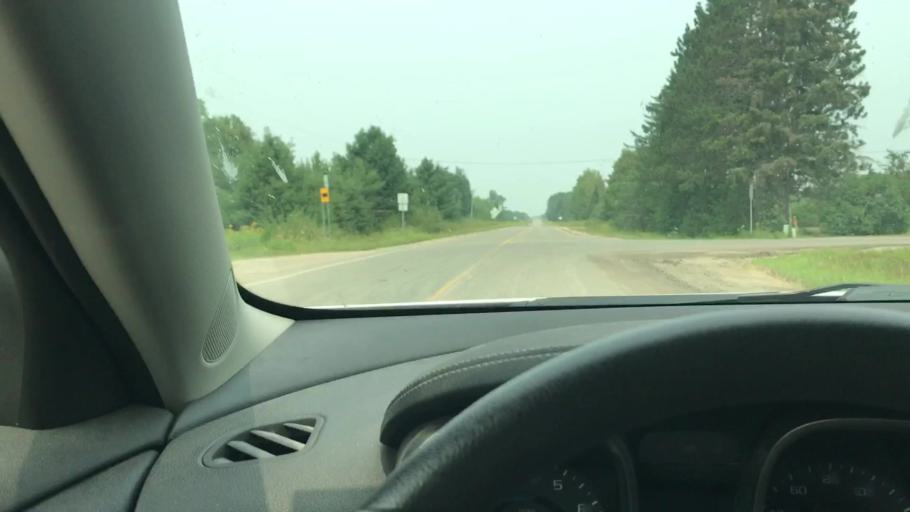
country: US
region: Minnesota
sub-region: Itasca County
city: Cohasset
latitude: 47.3679
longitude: -93.8804
